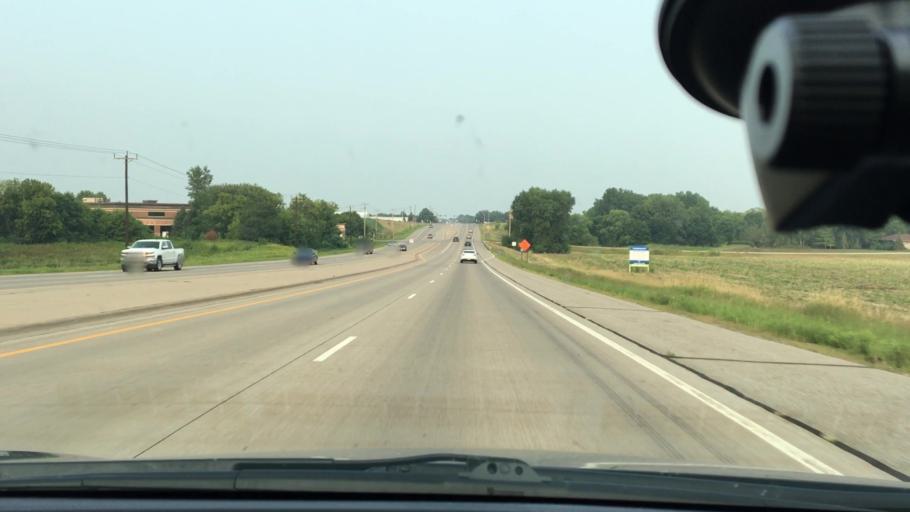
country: US
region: Minnesota
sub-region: Wright County
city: Saint Michael
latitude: 45.2117
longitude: -93.6330
